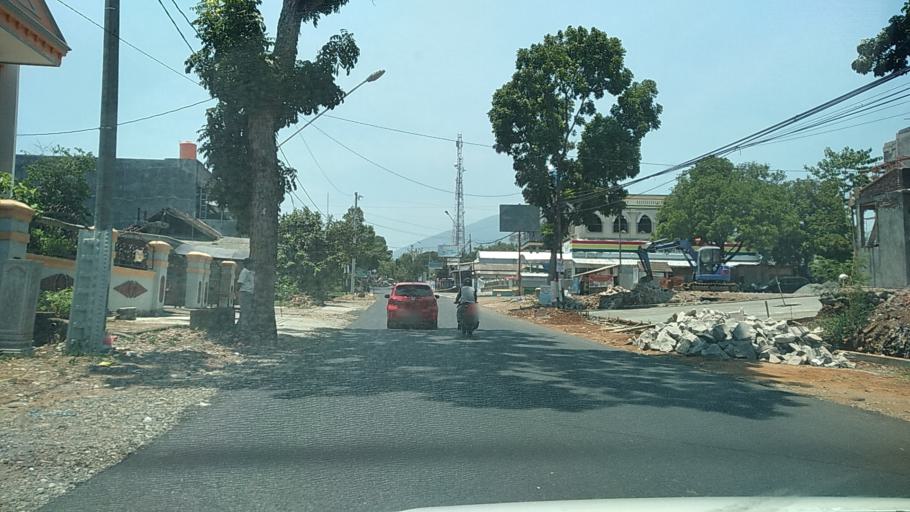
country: ID
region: Central Java
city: Ungaran
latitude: -7.0824
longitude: 110.3609
